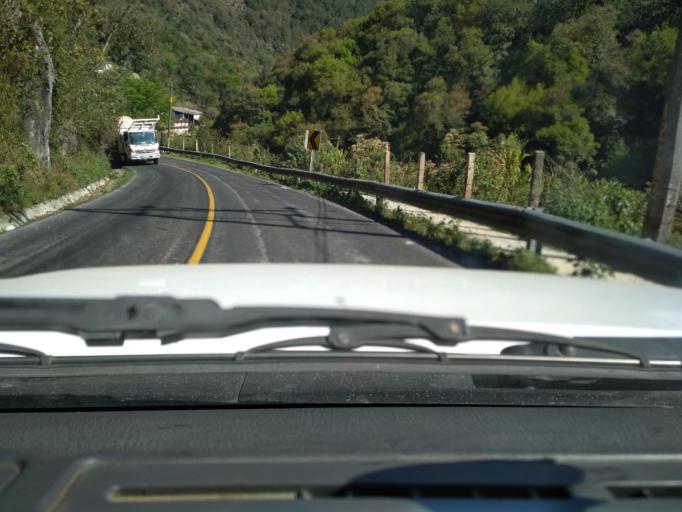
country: MX
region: Veracruz
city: Tequila
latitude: 18.7487
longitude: -97.0899
